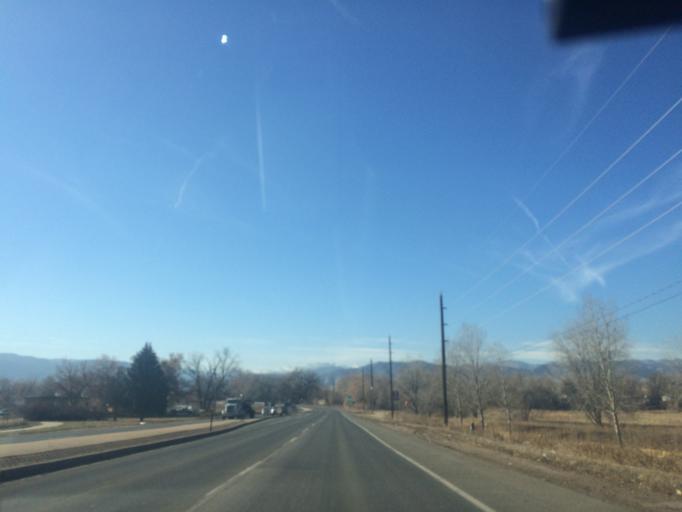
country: US
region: Colorado
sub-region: Boulder County
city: Boulder
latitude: 40.0293
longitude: -105.2191
